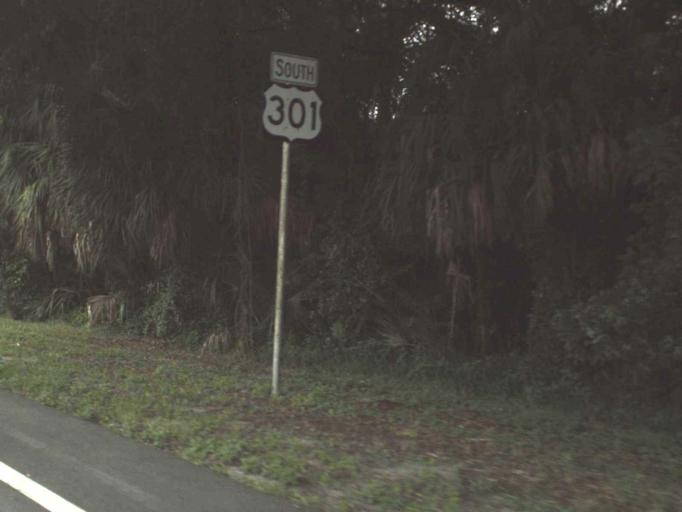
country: US
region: Florida
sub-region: Sumter County
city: Bushnell
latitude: 28.6109
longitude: -82.1381
